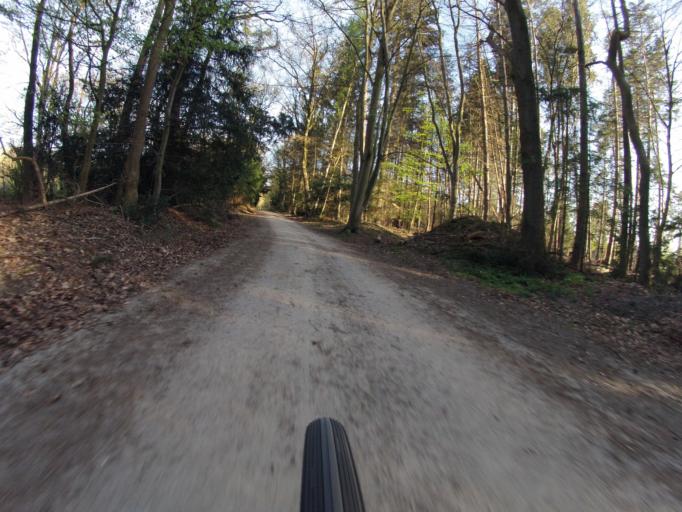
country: DE
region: Lower Saxony
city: Salzbergen
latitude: 52.3583
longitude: 7.3348
